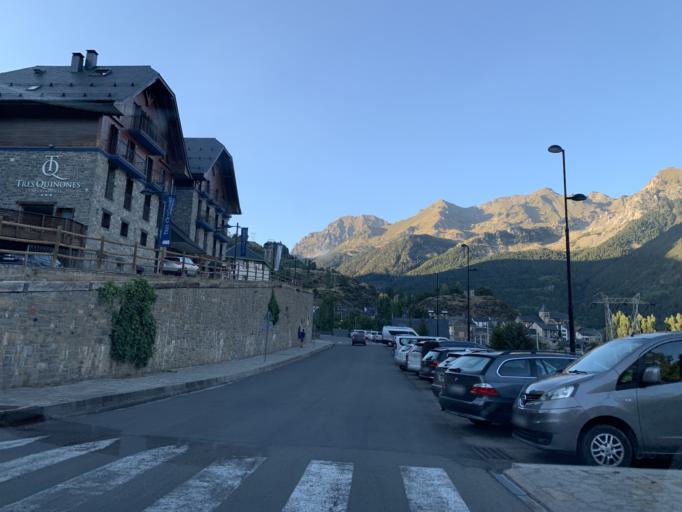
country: ES
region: Aragon
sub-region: Provincia de Huesca
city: Sallent de Gallego
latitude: 42.7692
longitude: -0.3347
